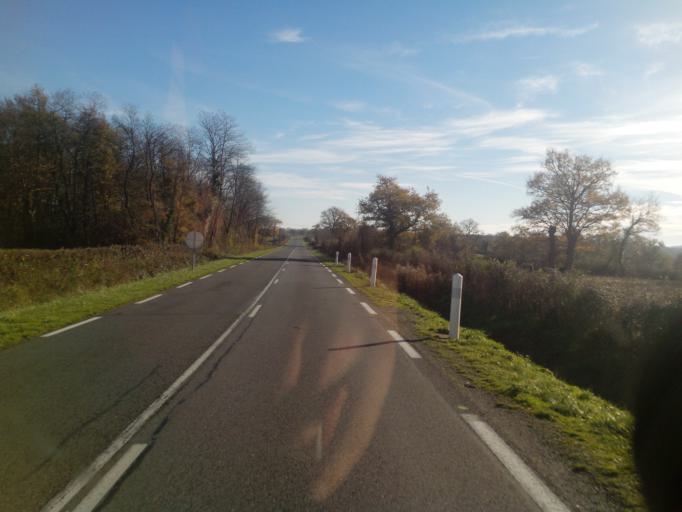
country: FR
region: Limousin
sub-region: Departement de la Haute-Vienne
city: Peyrat-de-Bellac
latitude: 46.1480
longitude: 0.9670
